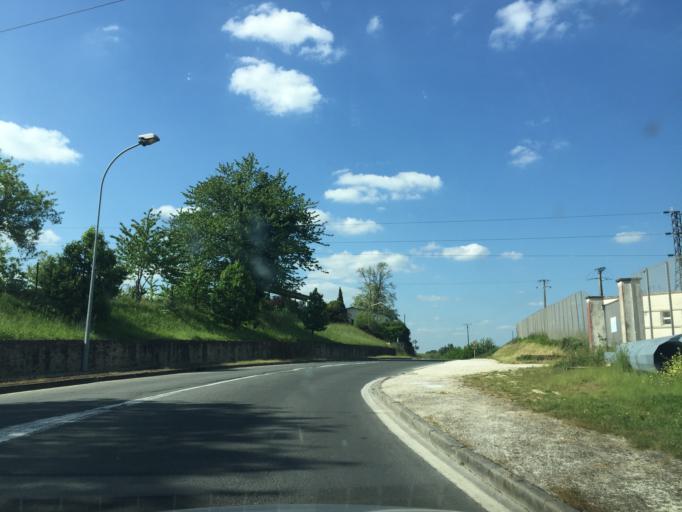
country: FR
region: Aquitaine
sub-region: Departement de la Gironde
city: La Reole
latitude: 44.5919
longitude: -0.0328
